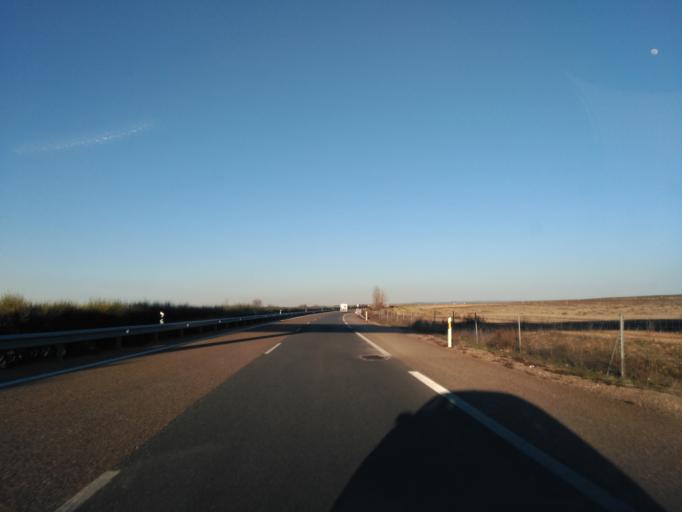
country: ES
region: Castille and Leon
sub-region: Provincia de Zamora
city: Castrillo de la Guarena
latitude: 41.2527
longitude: -5.2873
